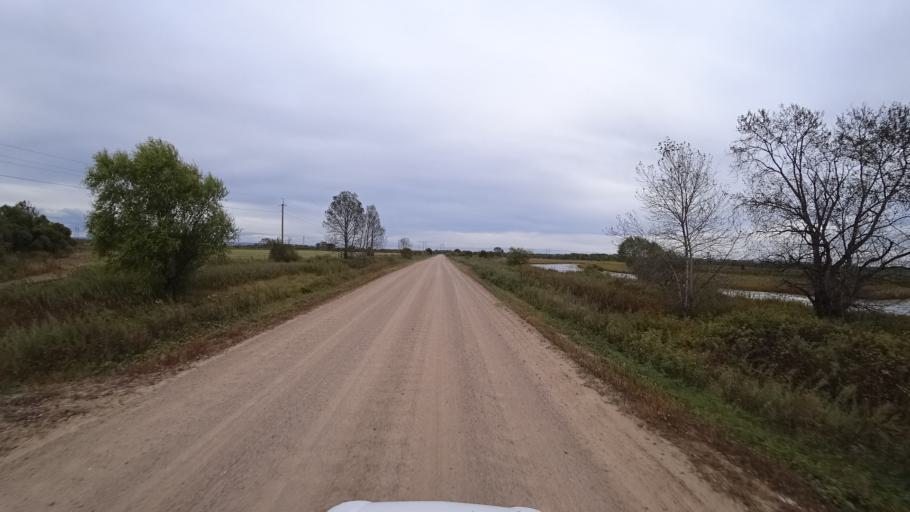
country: RU
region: Amur
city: Arkhara
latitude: 49.4307
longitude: 130.2371
